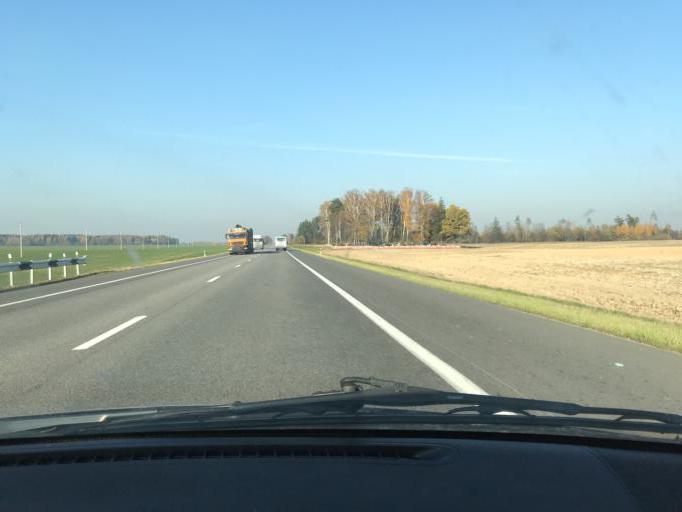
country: BY
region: Vitebsk
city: Balbasava
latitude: 54.3196
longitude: 30.4473
